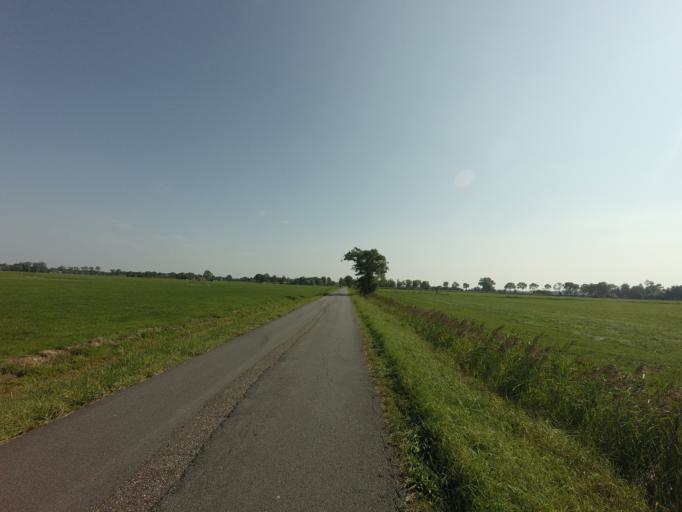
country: NL
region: Groningen
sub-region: Gemeente Zuidhorn
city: Zuidhorn
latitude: 53.2144
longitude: 6.4323
